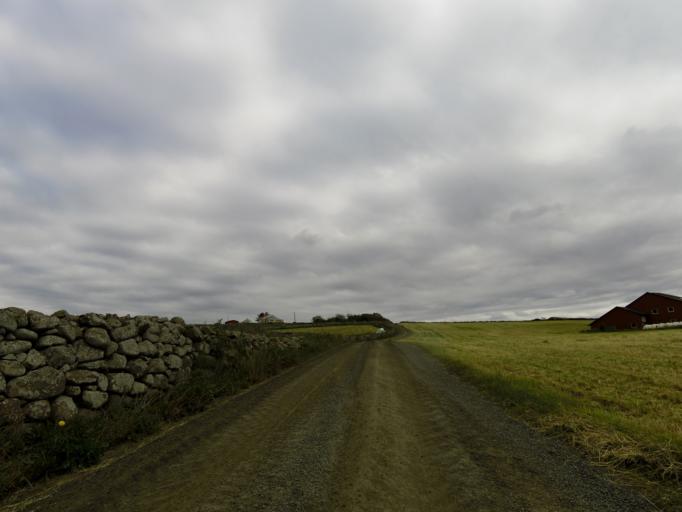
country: NO
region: Vest-Agder
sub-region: Farsund
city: Vestbygd
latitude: 58.1377
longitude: 6.6057
